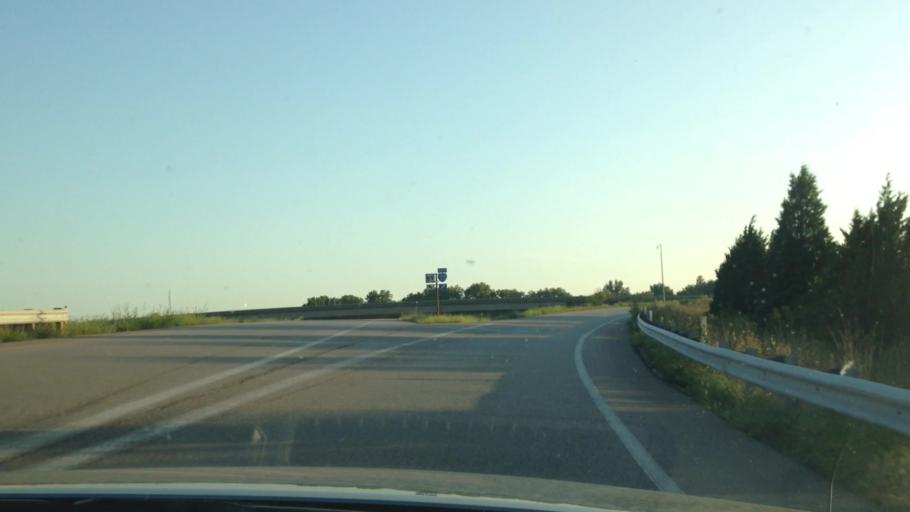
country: US
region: Missouri
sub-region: Clay County
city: Claycomo
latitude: 39.2080
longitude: -94.4920
